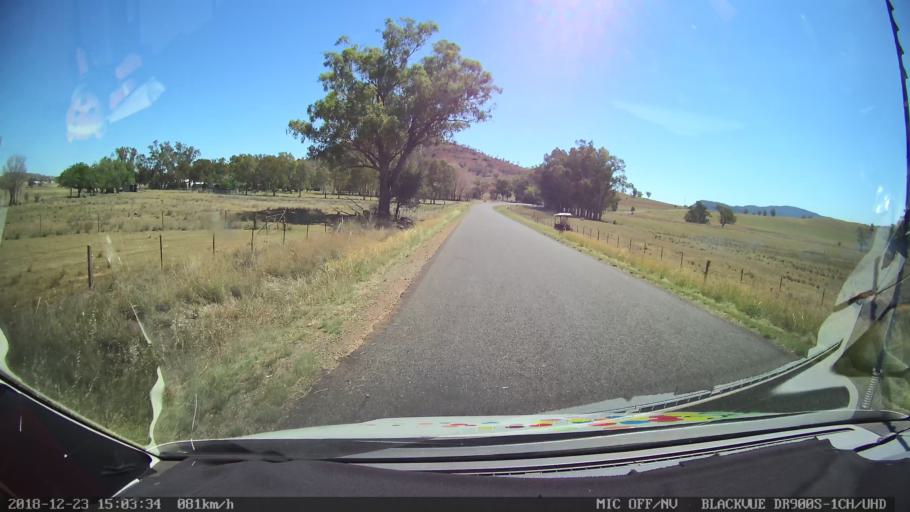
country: AU
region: New South Wales
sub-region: Tamworth Municipality
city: Manilla
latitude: -30.7396
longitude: 150.7636
